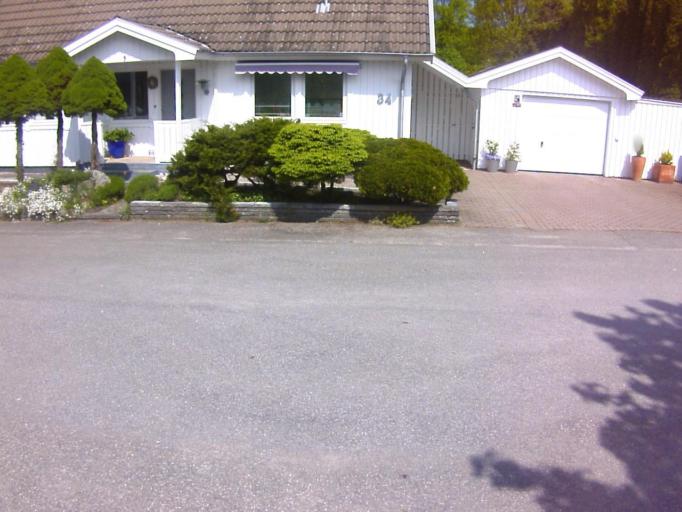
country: SE
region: Blekinge
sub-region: Solvesborgs Kommun
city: Soelvesborg
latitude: 56.0445
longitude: 14.5663
